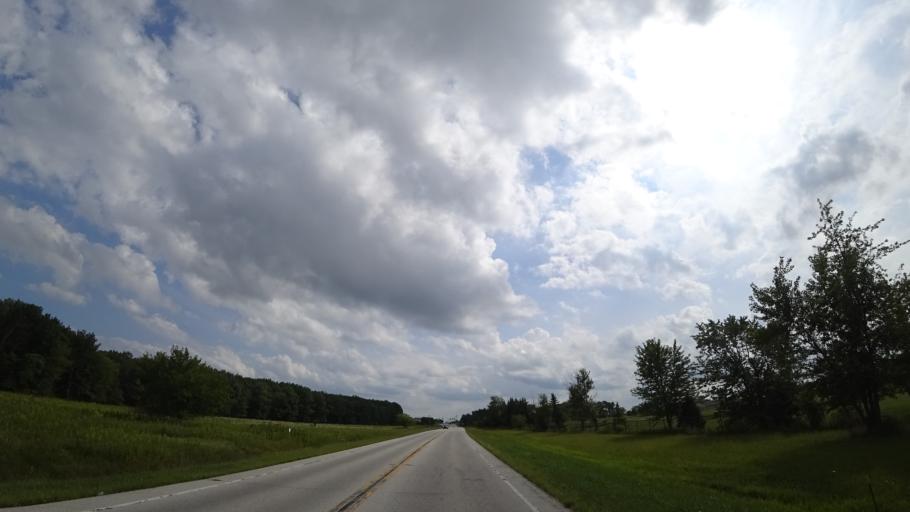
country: US
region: Illinois
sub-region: Will County
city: Frankfort Square
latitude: 41.5322
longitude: -87.7710
